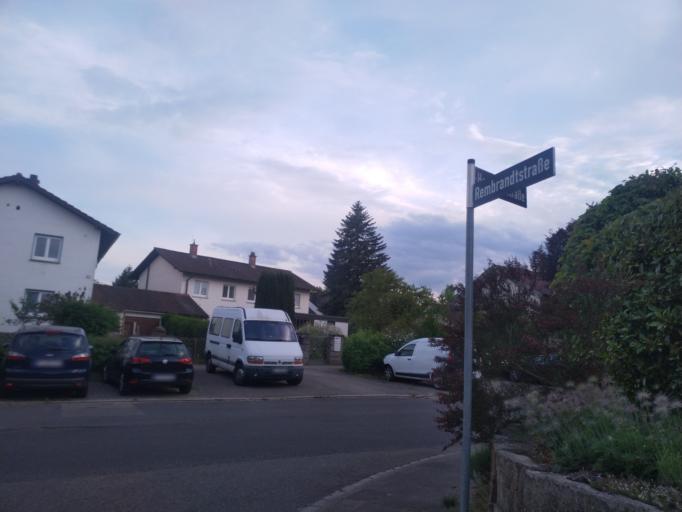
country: DE
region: Baden-Wuerttemberg
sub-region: Karlsruhe Region
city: Pforzheim
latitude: 48.8828
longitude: 8.6835
